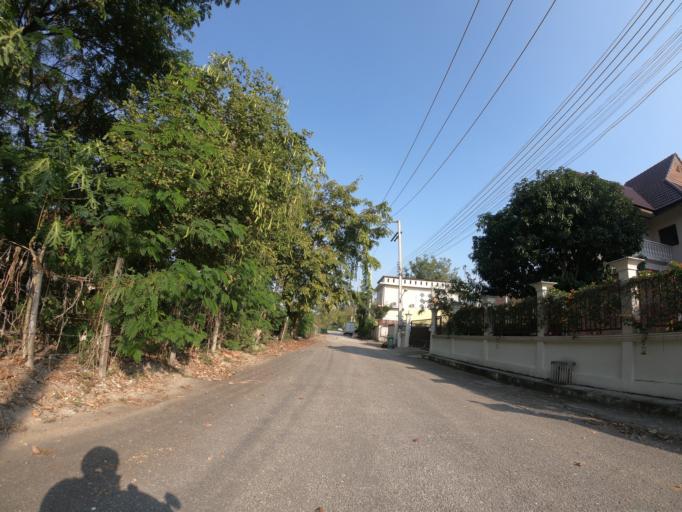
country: TH
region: Chiang Mai
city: San Sai
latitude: 18.8329
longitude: 99.0020
